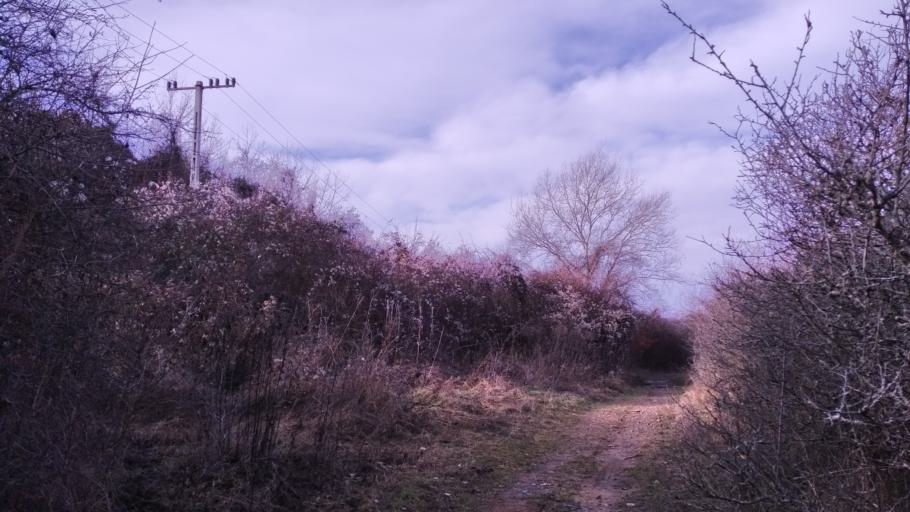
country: HU
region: Pest
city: Pomaz
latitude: 47.6213
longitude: 19.0207
